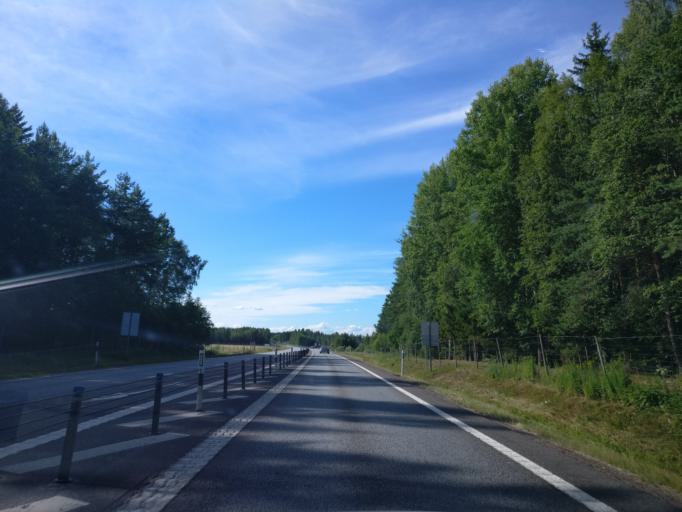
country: SE
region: Vaermland
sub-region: Kils Kommun
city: Kil
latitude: 59.4788
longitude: 13.3587
